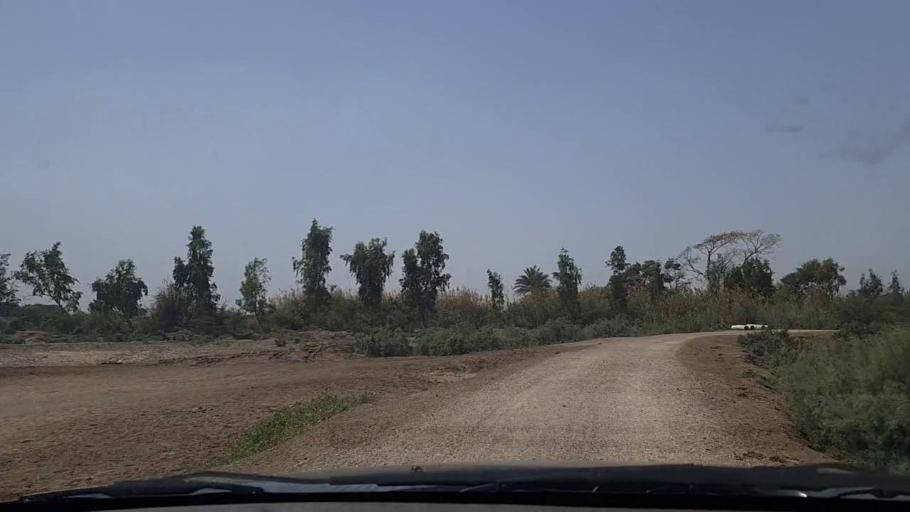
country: PK
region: Sindh
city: Mirpur Sakro
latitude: 24.3201
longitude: 67.6825
